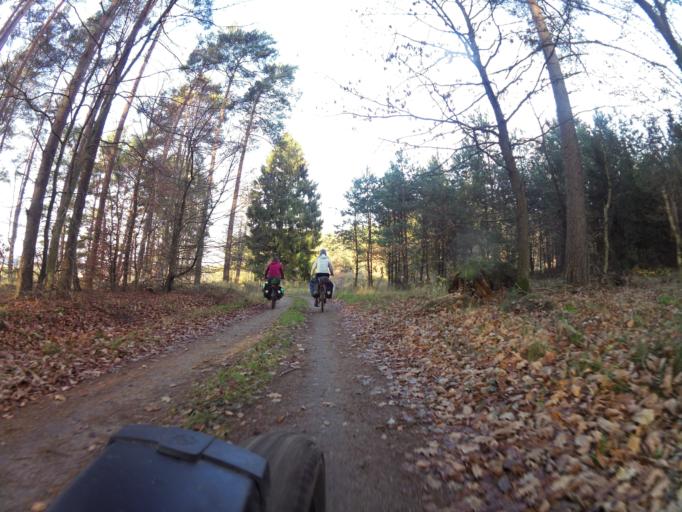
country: PL
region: West Pomeranian Voivodeship
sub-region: Powiat koszalinski
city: Polanow
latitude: 54.0962
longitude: 16.6484
